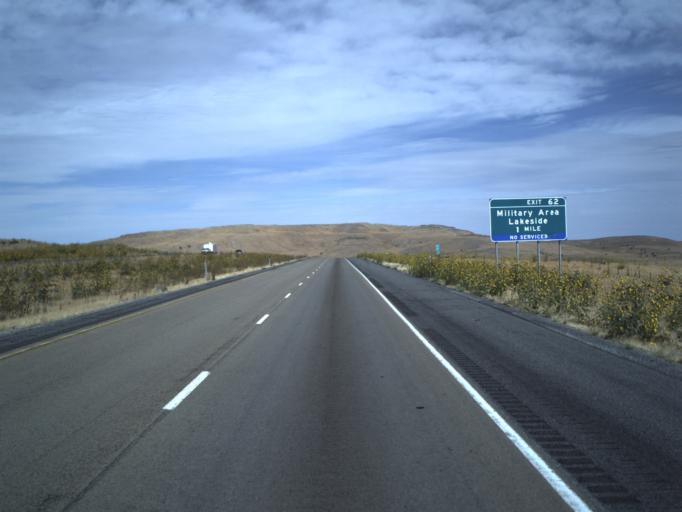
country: US
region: Utah
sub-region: Tooele County
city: Grantsville
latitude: 40.8179
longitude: -112.8818
